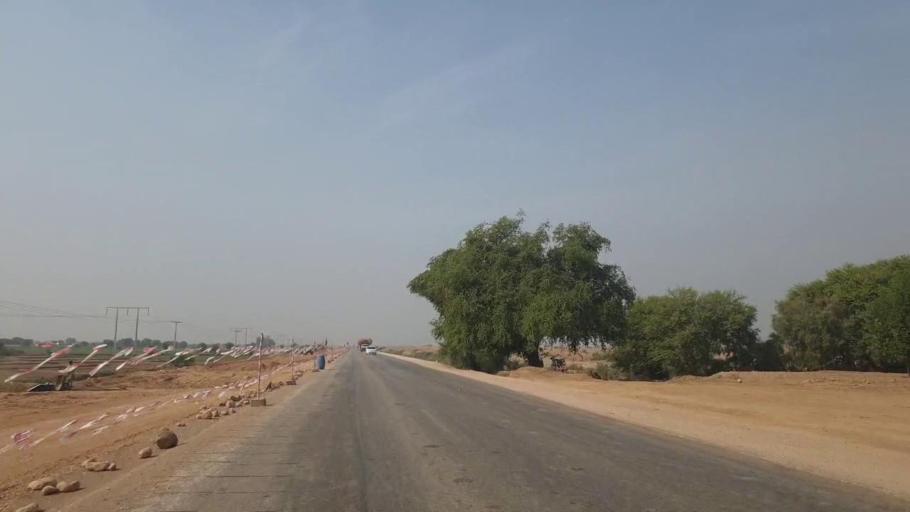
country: PK
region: Sindh
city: Sann
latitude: 26.1344
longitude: 68.0452
